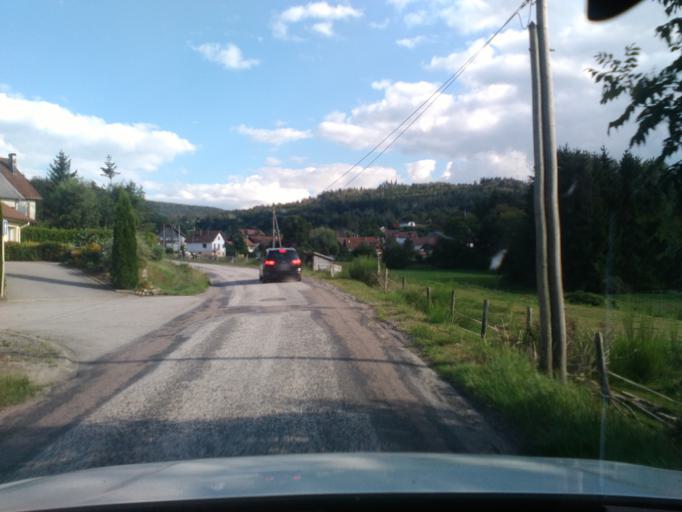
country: FR
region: Lorraine
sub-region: Departement des Vosges
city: Anould
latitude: 48.1535
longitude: 6.9199
